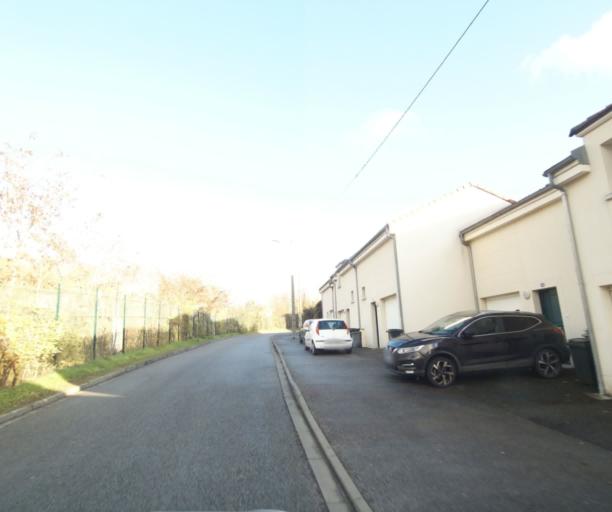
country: FR
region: Ile-de-France
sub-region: Departement des Yvelines
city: Meulan-en-Yvelines
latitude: 49.0093
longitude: 1.9328
